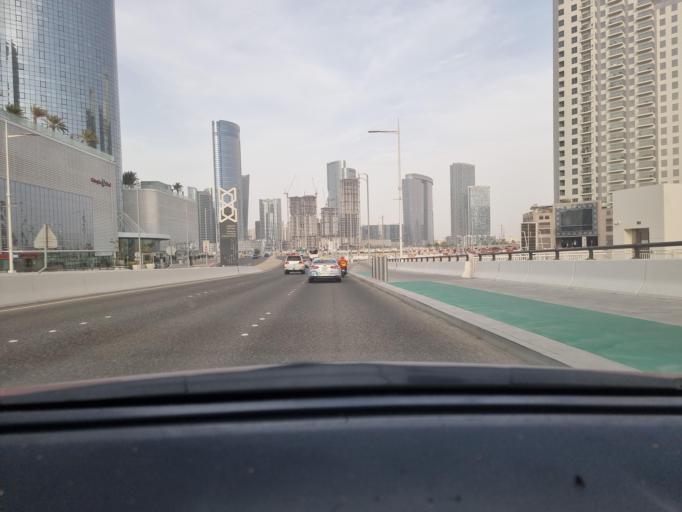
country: AE
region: Abu Dhabi
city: Abu Dhabi
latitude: 24.4984
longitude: 54.3930
